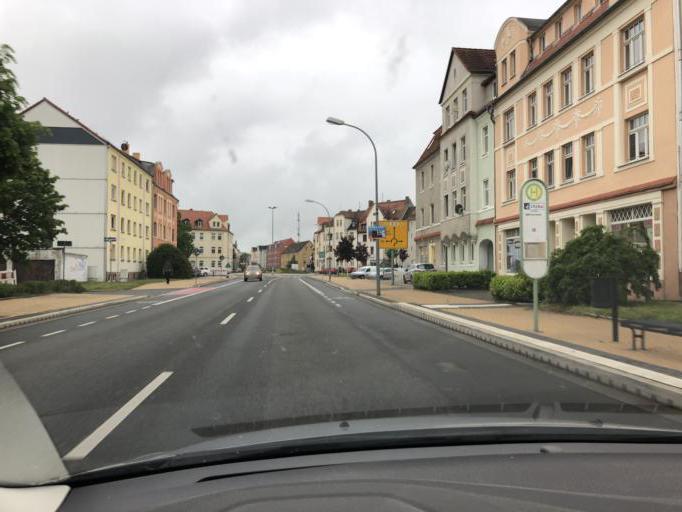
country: DE
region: Saxony
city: Delitzsch
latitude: 51.5318
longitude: 12.3361
